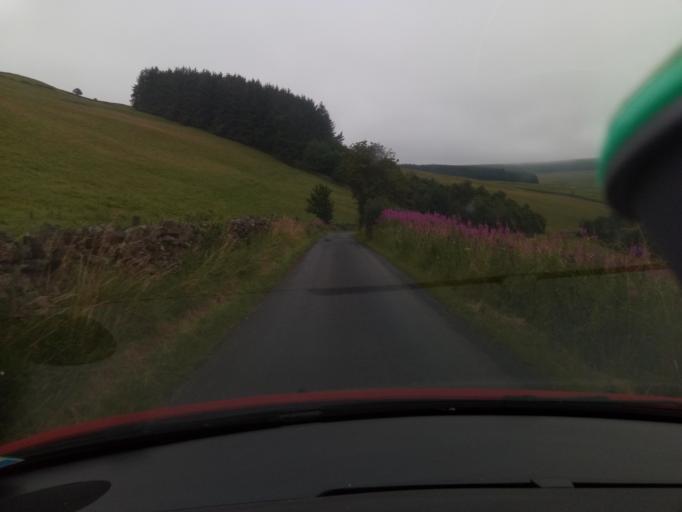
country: GB
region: Scotland
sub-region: The Scottish Borders
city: Galashiels
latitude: 55.7003
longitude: -2.8895
